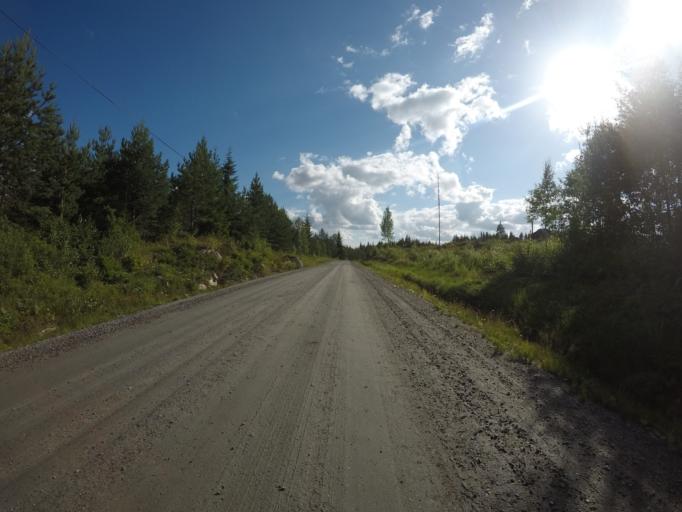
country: SE
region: OErebro
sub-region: Hallefors Kommun
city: Haellefors
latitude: 59.9075
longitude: 14.5936
